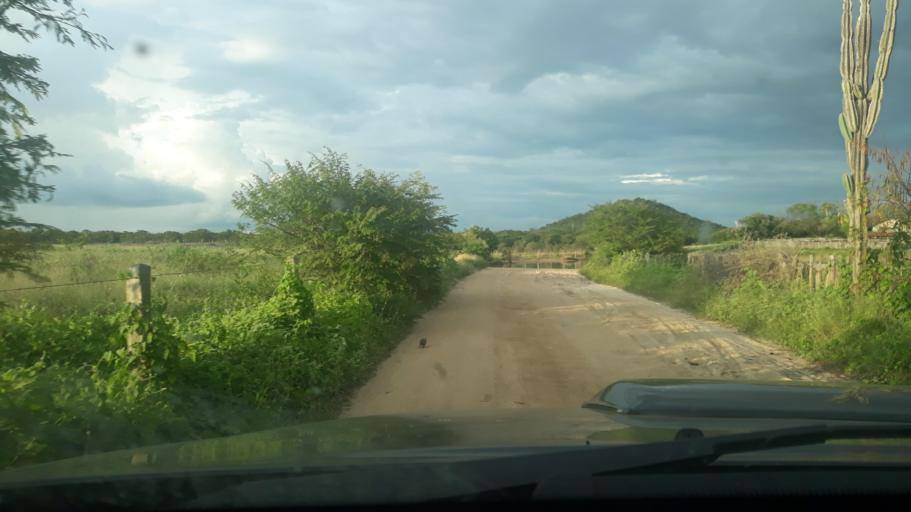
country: BR
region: Bahia
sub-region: Riacho De Santana
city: Riacho de Santana
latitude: -13.9104
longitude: -42.9468
